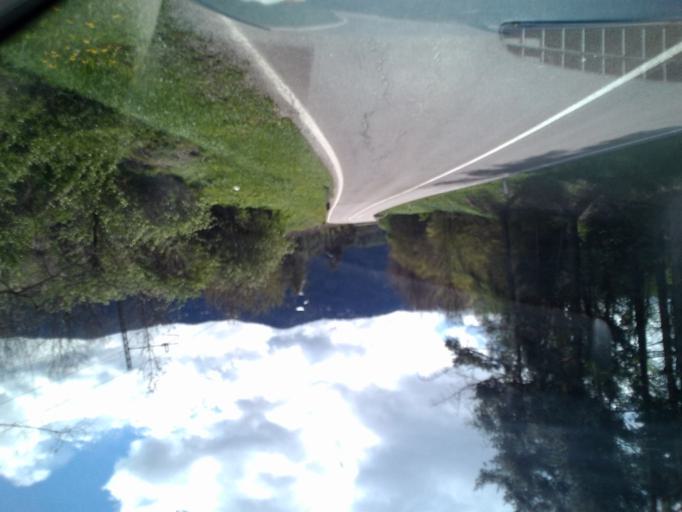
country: IT
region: Trentino-Alto Adige
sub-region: Bolzano
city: Brunico
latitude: 46.7953
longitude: 11.9516
